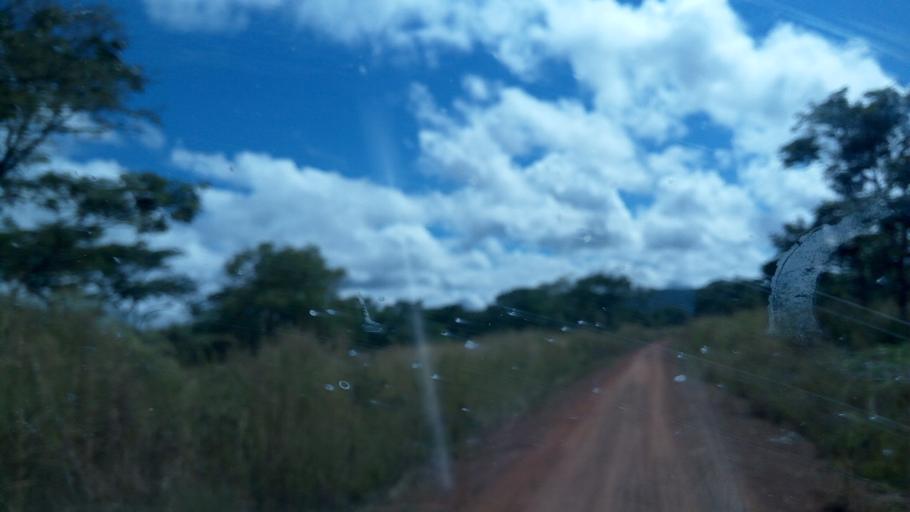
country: ZM
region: Northern
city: Kaputa
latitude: -8.2428
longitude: 29.0353
